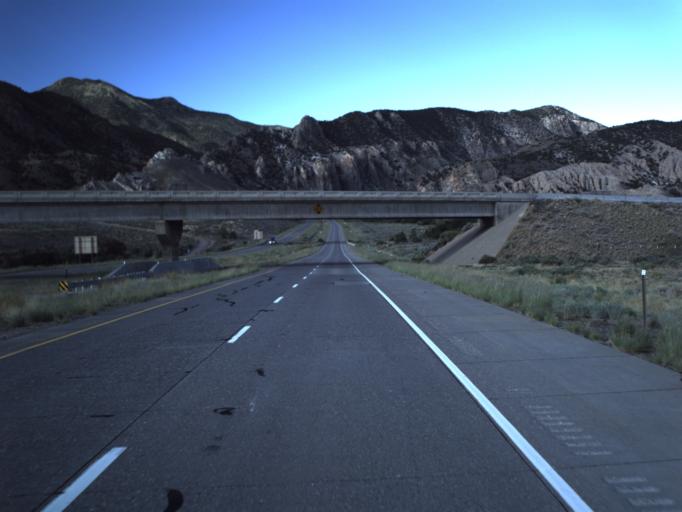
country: US
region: Utah
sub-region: Sevier County
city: Monroe
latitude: 38.5908
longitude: -112.2695
